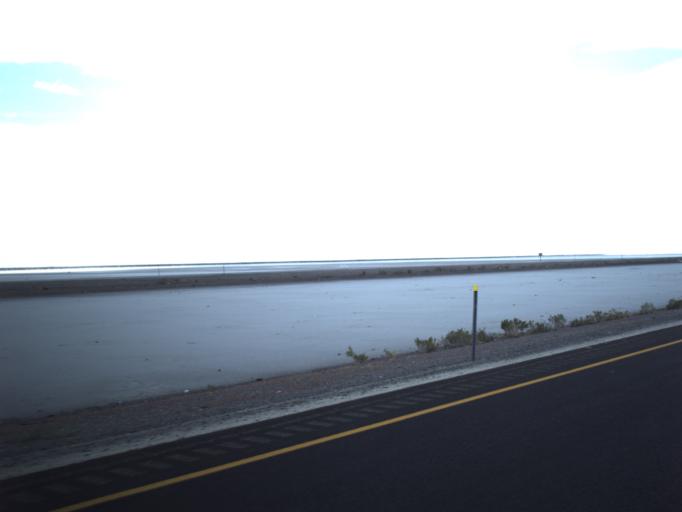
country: US
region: Utah
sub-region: Tooele County
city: Wendover
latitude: 40.7320
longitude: -113.5485
